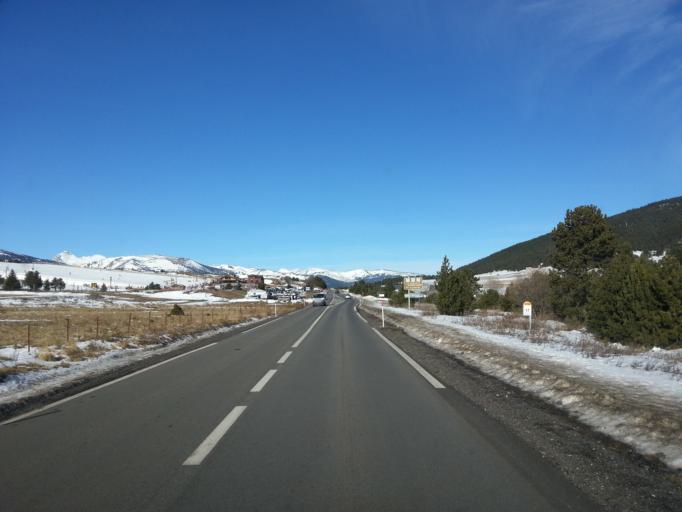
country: ES
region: Catalonia
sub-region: Provincia de Girona
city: Llivia
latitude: 42.5395
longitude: 2.1206
